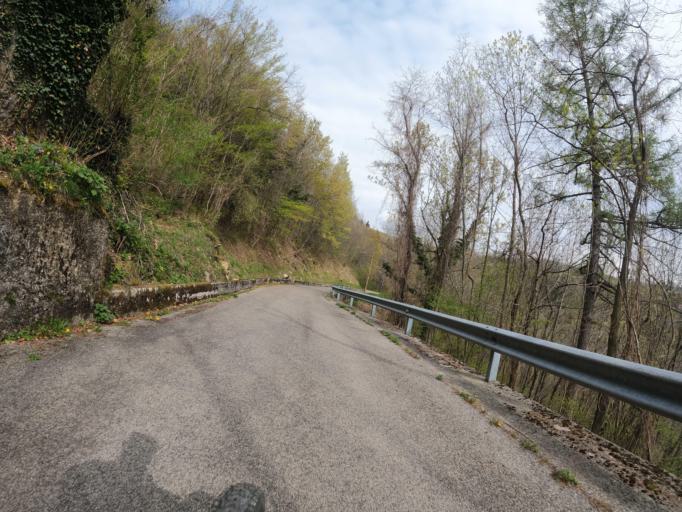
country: IT
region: Friuli Venezia Giulia
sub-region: Provincia di Udine
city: Clodig
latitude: 46.1390
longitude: 13.5994
